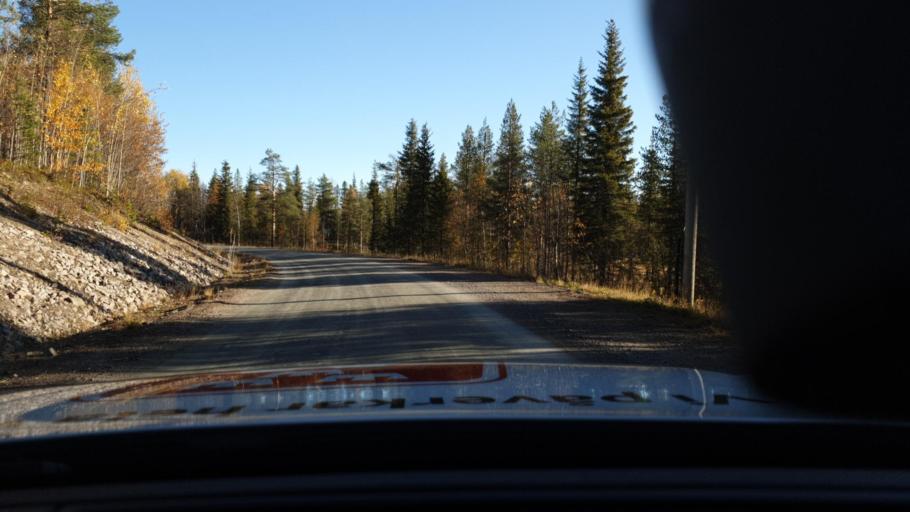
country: SE
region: Norrbotten
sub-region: Gallivare Kommun
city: Malmberget
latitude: 67.3873
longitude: 21.7039
